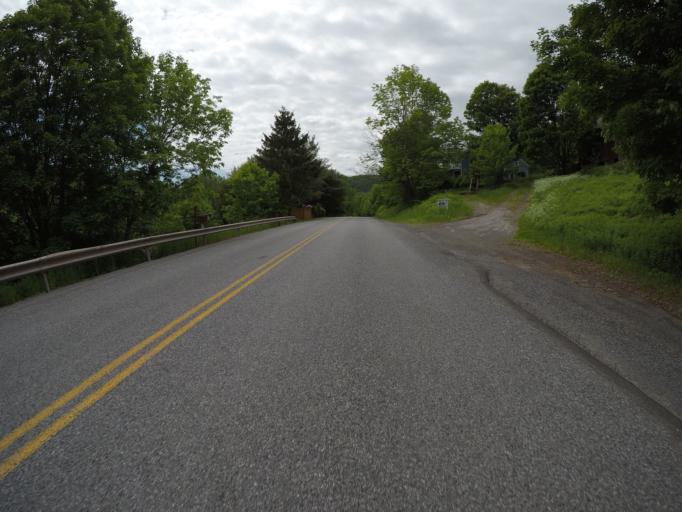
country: US
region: New York
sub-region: Delaware County
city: Stamford
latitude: 42.1890
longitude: -74.5835
